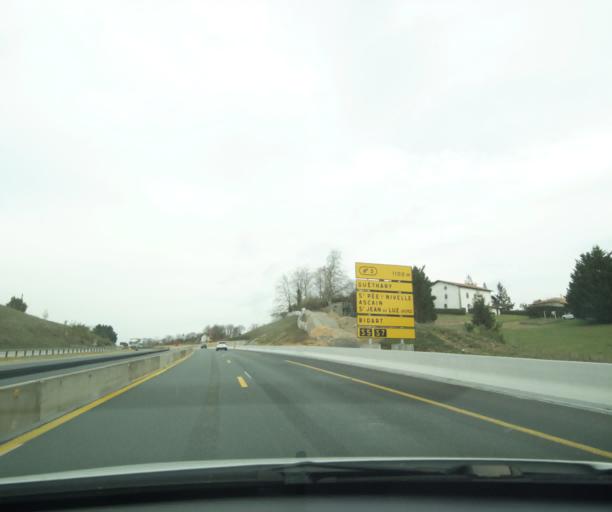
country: FR
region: Aquitaine
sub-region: Departement des Pyrenees-Atlantiques
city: Saint-Jean-de-Luz
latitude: 43.3917
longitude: -1.6386
